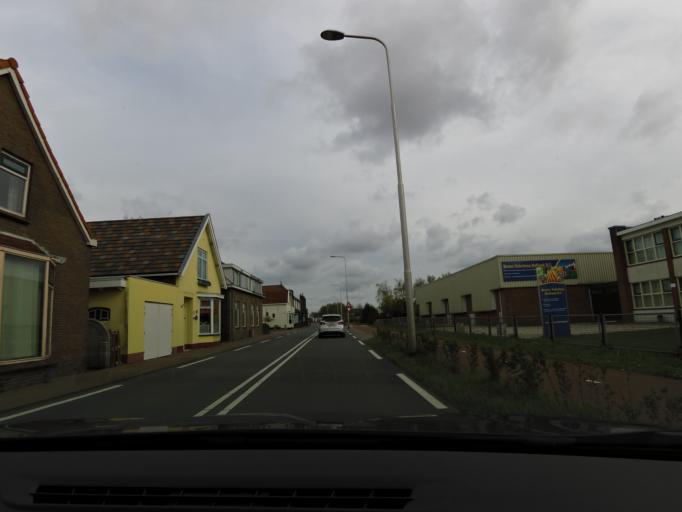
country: NL
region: South Holland
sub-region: Gemeente Teylingen
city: Sassenheim
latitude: 52.2396
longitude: 4.5037
